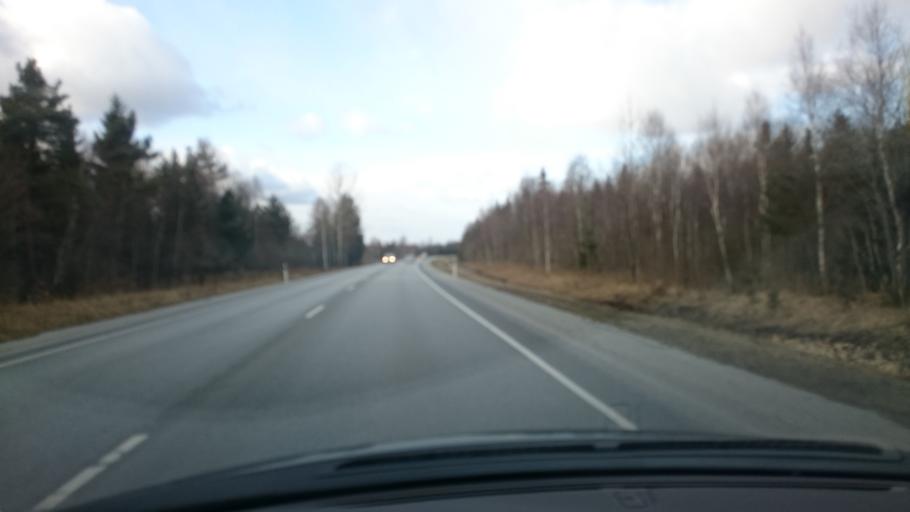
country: EE
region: Harju
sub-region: Nissi vald
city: Riisipere
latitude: 59.1577
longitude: 24.3417
